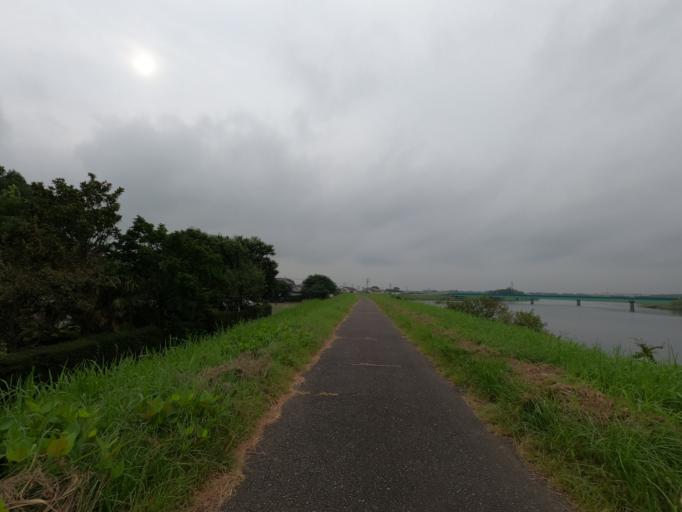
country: JP
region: Ibaraki
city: Moriya
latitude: 35.9497
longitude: 140.0267
